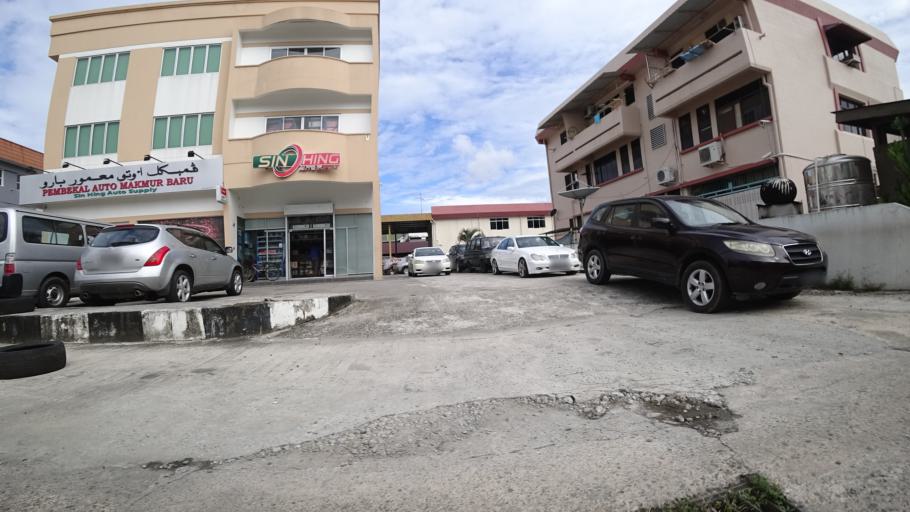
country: BN
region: Brunei and Muara
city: Bandar Seri Begawan
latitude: 4.9086
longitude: 114.9241
